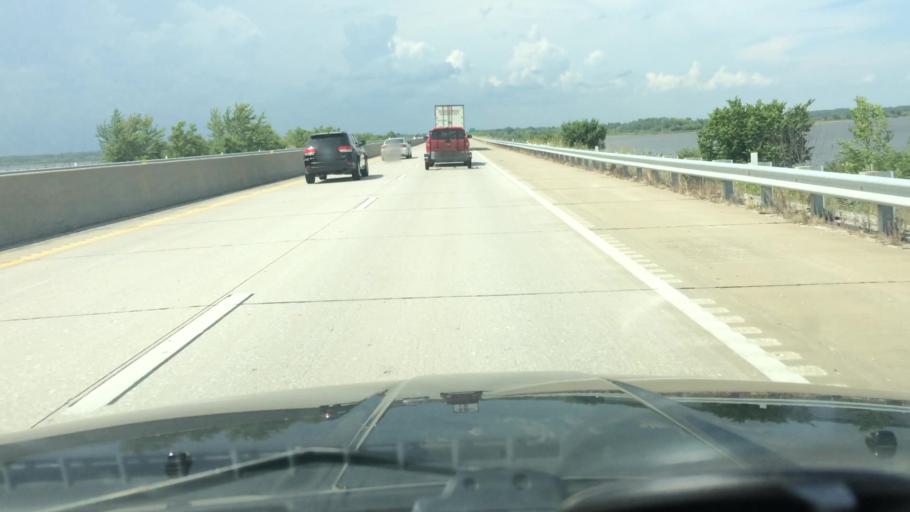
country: US
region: Missouri
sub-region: Henry County
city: Clinton
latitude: 38.3153
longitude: -93.7581
